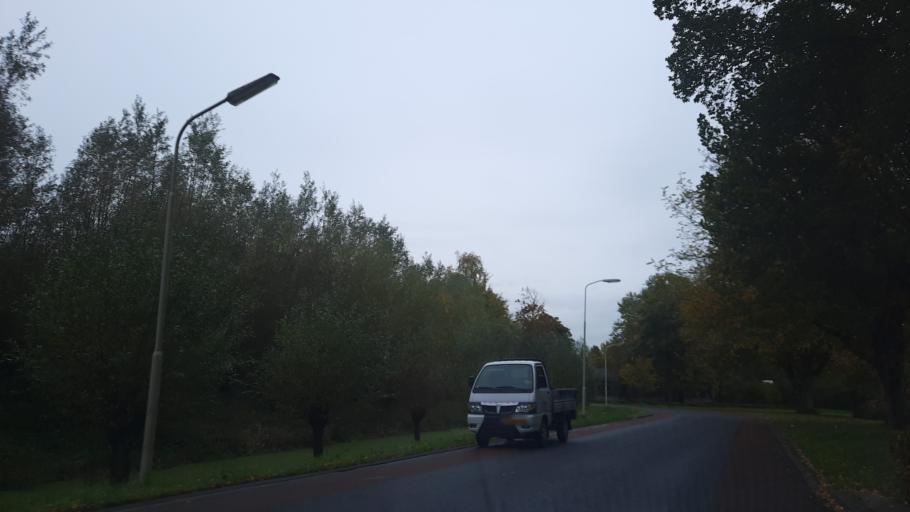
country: NL
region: South Holland
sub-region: Gemeente Gorinchem
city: Gorinchem
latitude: 51.8321
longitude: 4.9845
